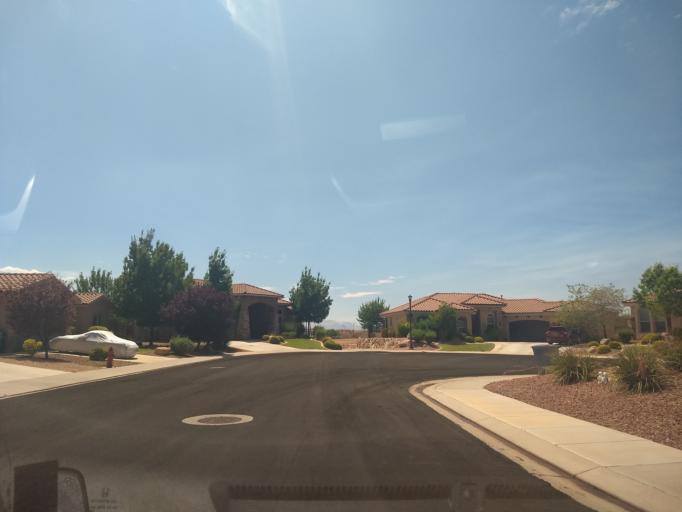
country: US
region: Utah
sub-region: Washington County
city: Washington
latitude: 37.1430
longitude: -113.4824
